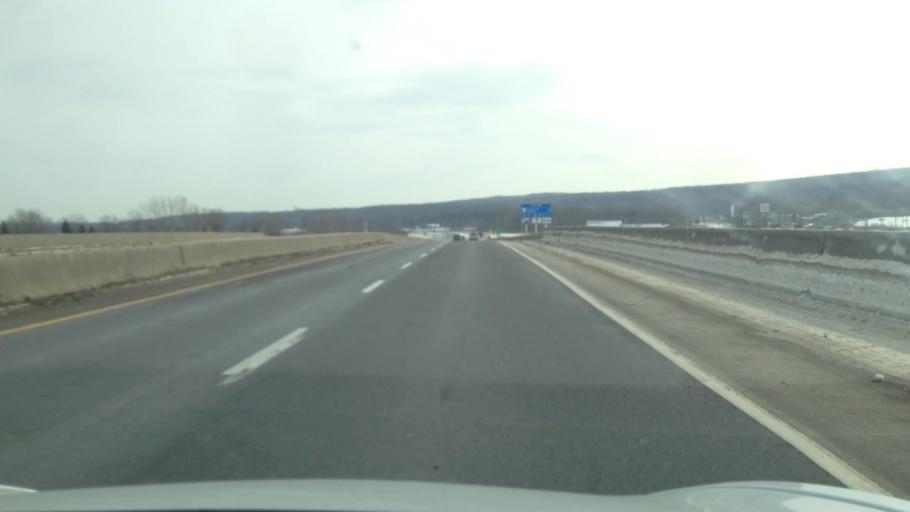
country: CA
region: Quebec
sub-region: Monteregie
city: Rigaud
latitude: 45.4819
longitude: -74.2879
